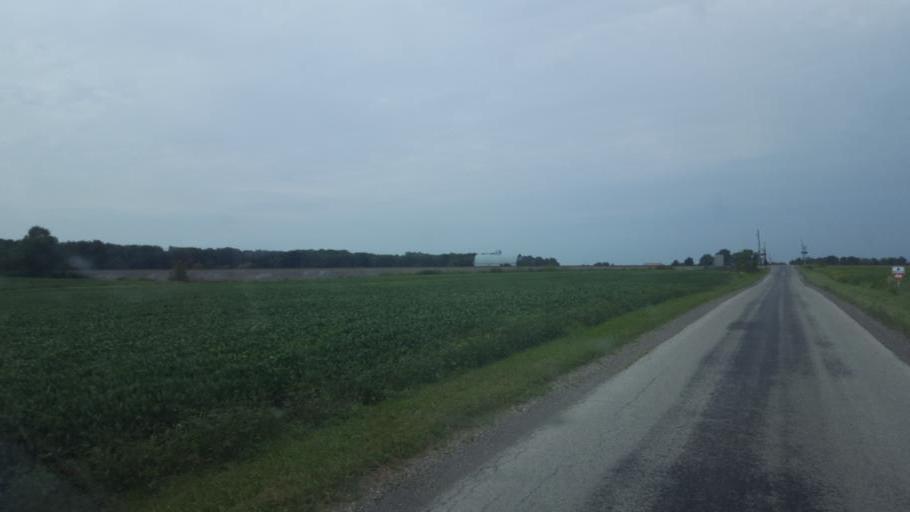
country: US
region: Ohio
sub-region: Marion County
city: Marion
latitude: 40.5131
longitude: -83.1111
